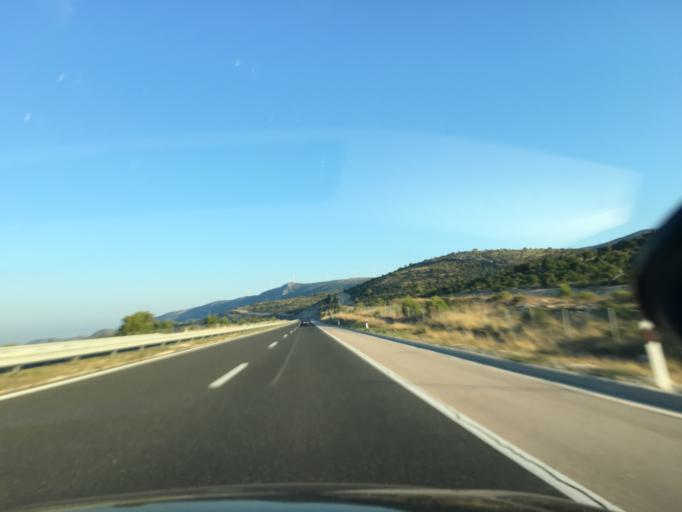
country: HR
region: Sibensko-Kniniska
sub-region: Grad Sibenik
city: Brodarica
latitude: 43.7144
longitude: 15.9887
